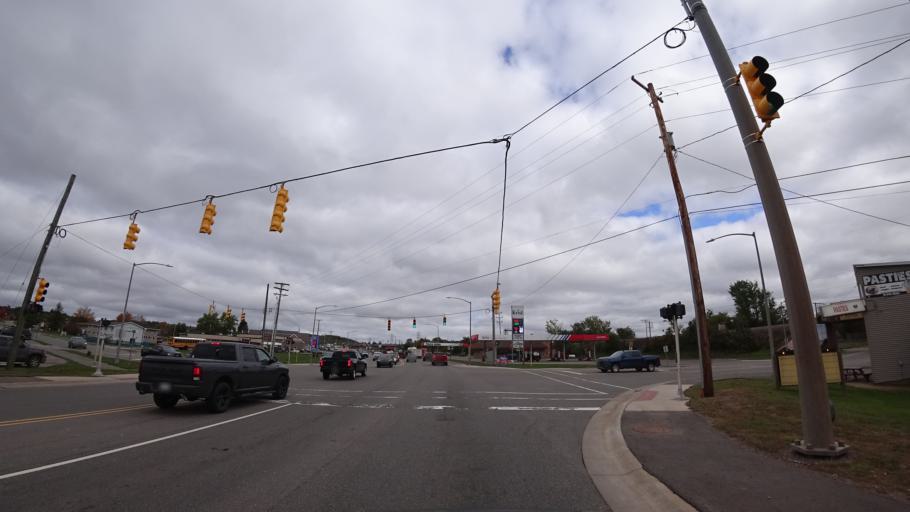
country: US
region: Michigan
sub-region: Marquette County
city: Negaunee
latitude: 46.5066
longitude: -87.6131
